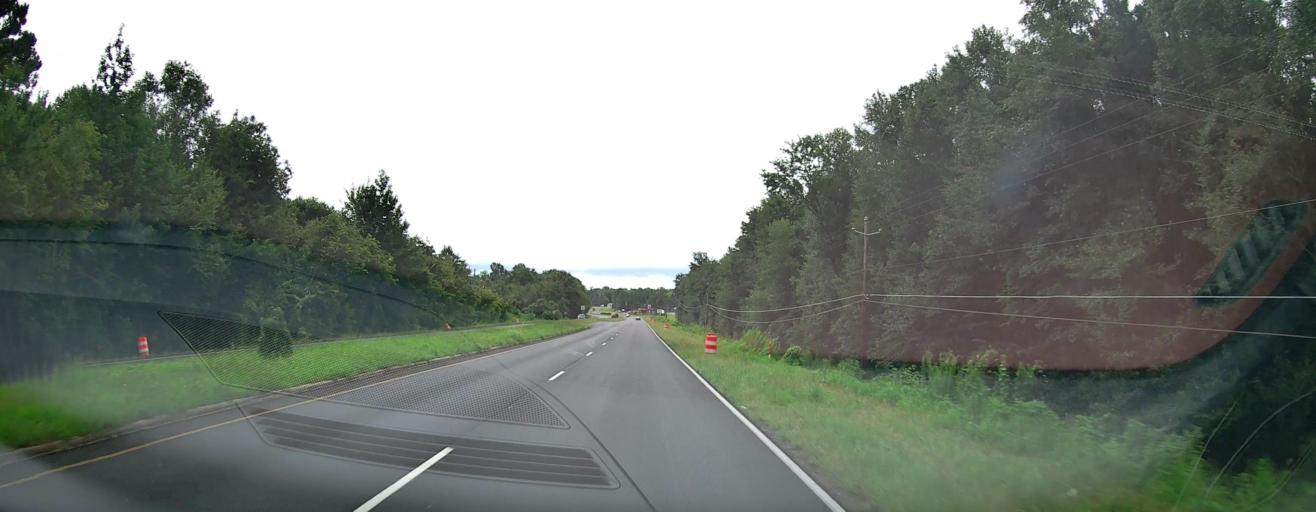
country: US
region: Georgia
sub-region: Bibb County
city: Macon
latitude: 32.8428
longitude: -83.5880
